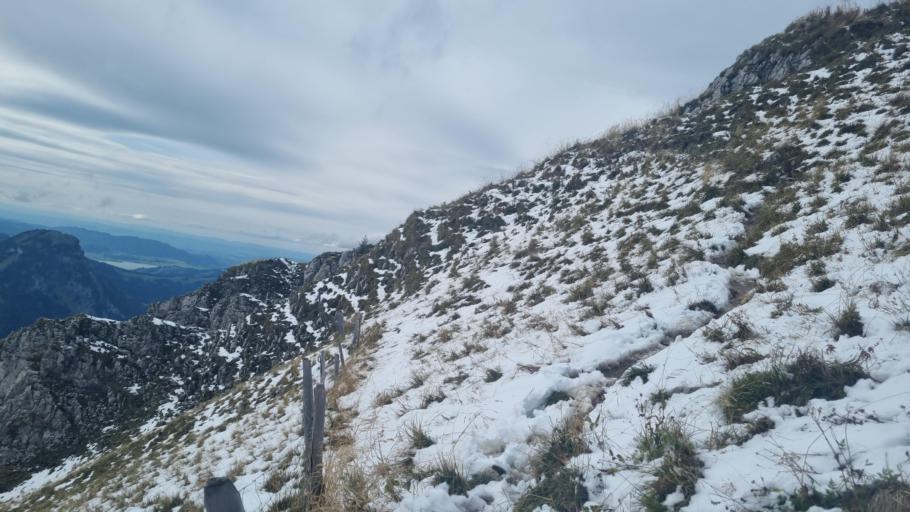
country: CH
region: Schwyz
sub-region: Bezirk March
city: Vorderthal
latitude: 47.1004
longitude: 8.9583
